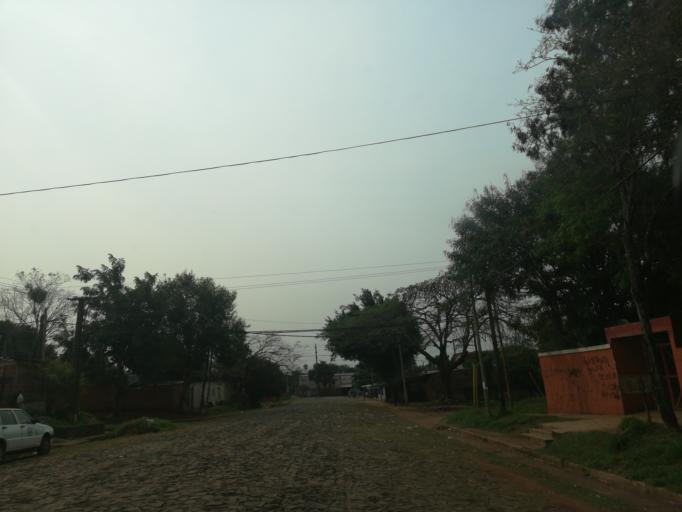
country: AR
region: Misiones
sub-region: Departamento de Capital
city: Posadas
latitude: -27.3747
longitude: -55.9382
